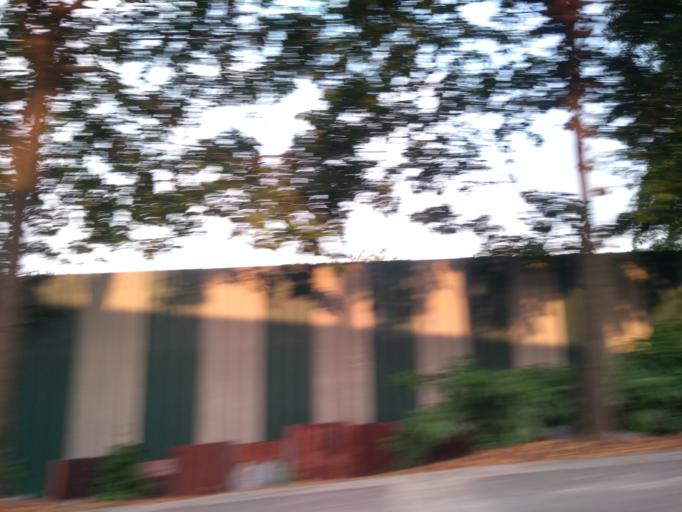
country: MY
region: Kuala Lumpur
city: Kuala Lumpur
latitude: 3.1323
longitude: 101.7041
